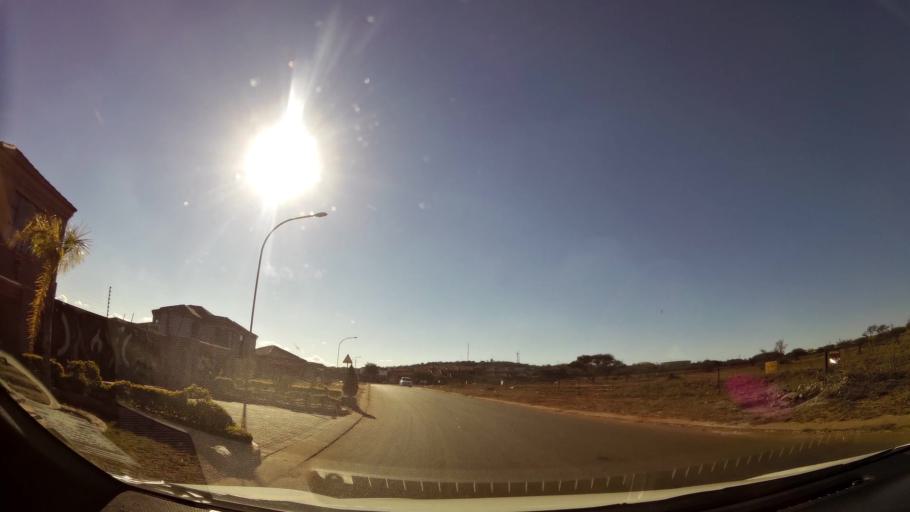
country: ZA
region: Limpopo
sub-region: Capricorn District Municipality
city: Polokwane
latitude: -23.9028
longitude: 29.5060
